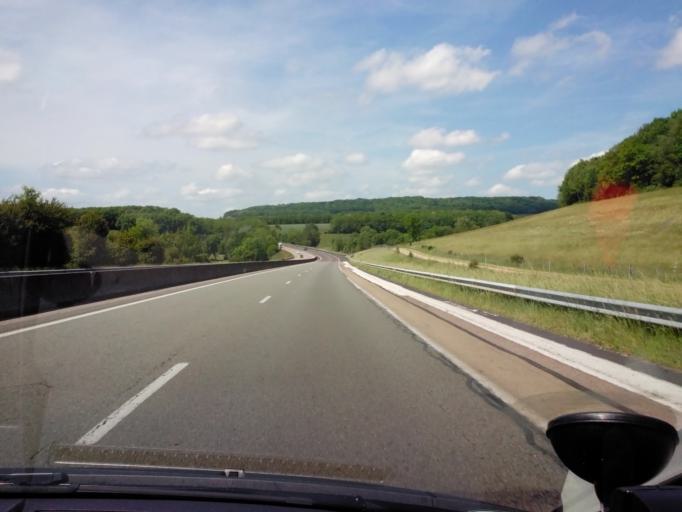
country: FR
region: Champagne-Ardenne
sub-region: Departement de la Haute-Marne
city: Avrecourt
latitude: 47.9596
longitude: 5.4571
